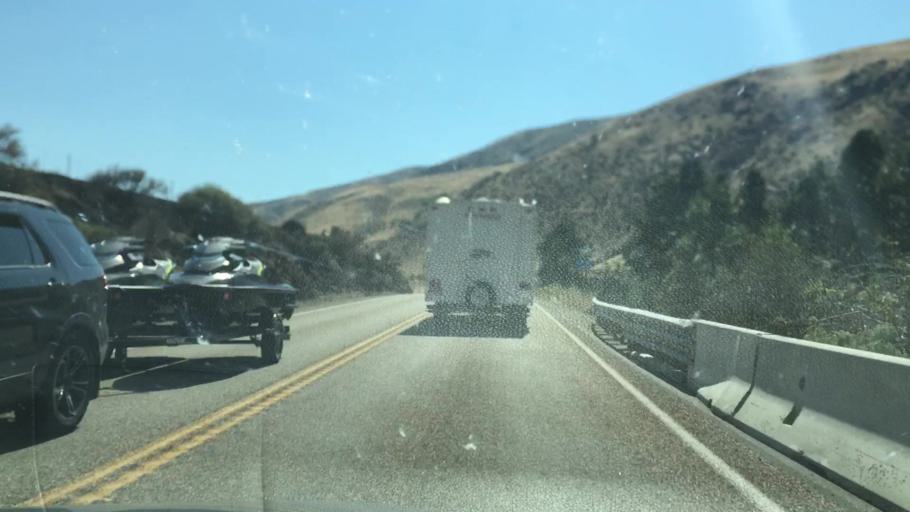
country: US
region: Idaho
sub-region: Gem County
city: Emmett
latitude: 44.0066
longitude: -116.1778
